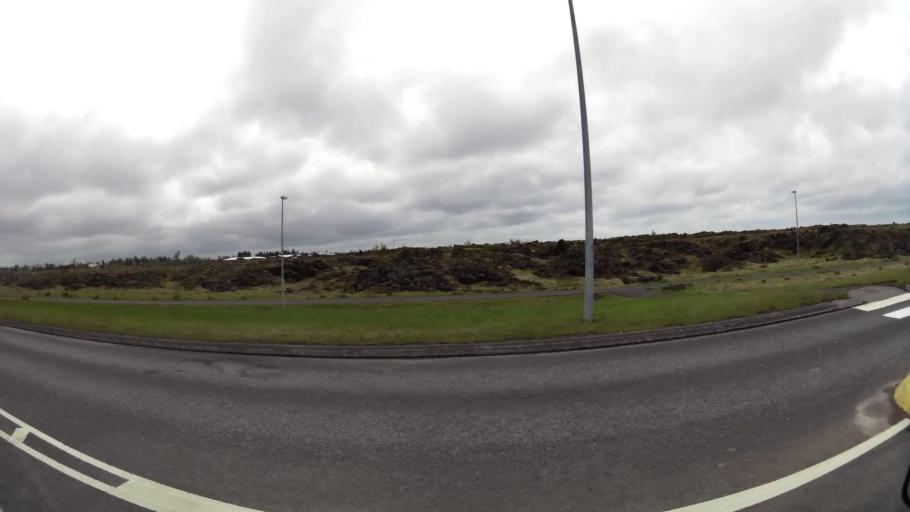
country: IS
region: Capital Region
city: Hafnarfjoerdur
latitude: 64.0890
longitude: -21.9534
